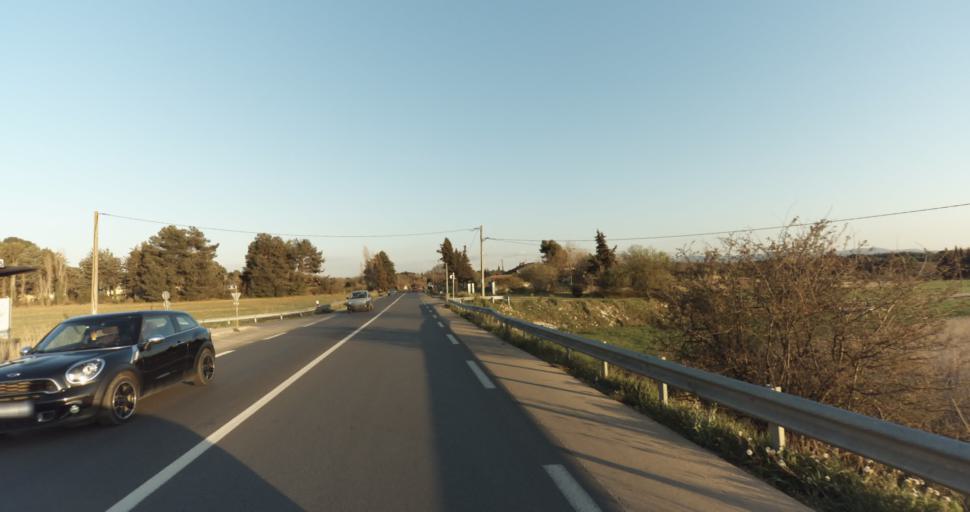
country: FR
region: Provence-Alpes-Cote d'Azur
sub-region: Departement des Bouches-du-Rhone
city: Eguilles
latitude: 43.5398
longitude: 5.3779
